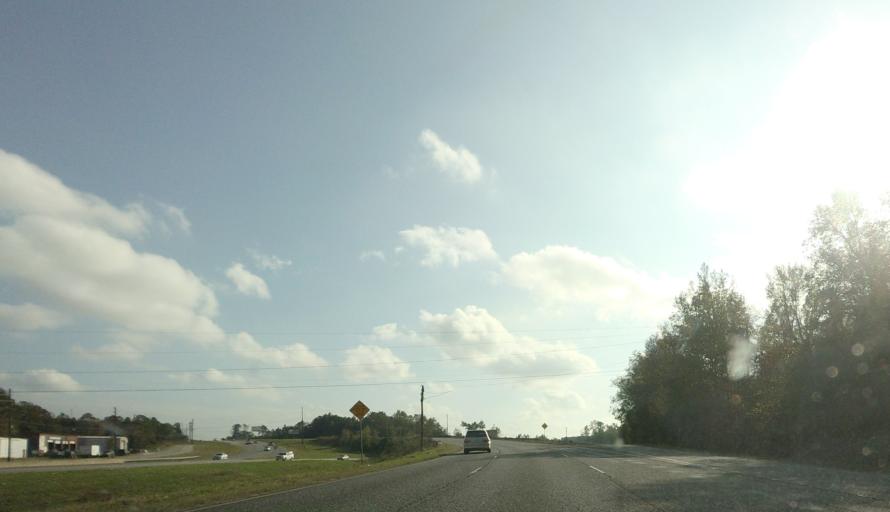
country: US
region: Georgia
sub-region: Bibb County
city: Macon
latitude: 32.7583
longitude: -83.6621
